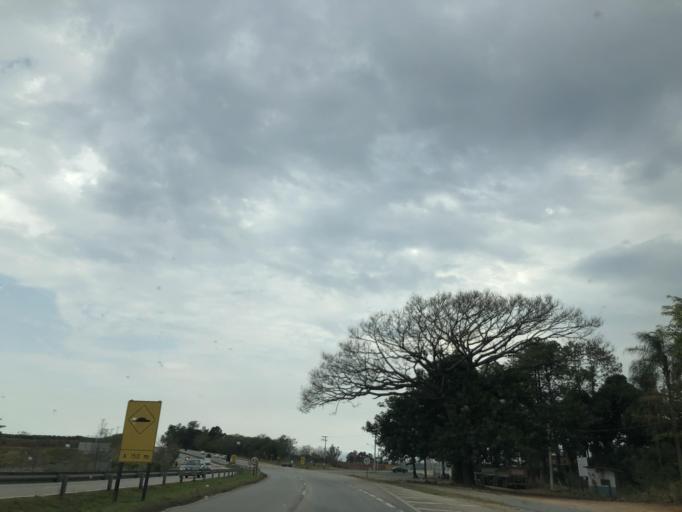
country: BR
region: Sao Paulo
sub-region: Votorantim
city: Votorantim
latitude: -23.5767
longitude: -47.5150
